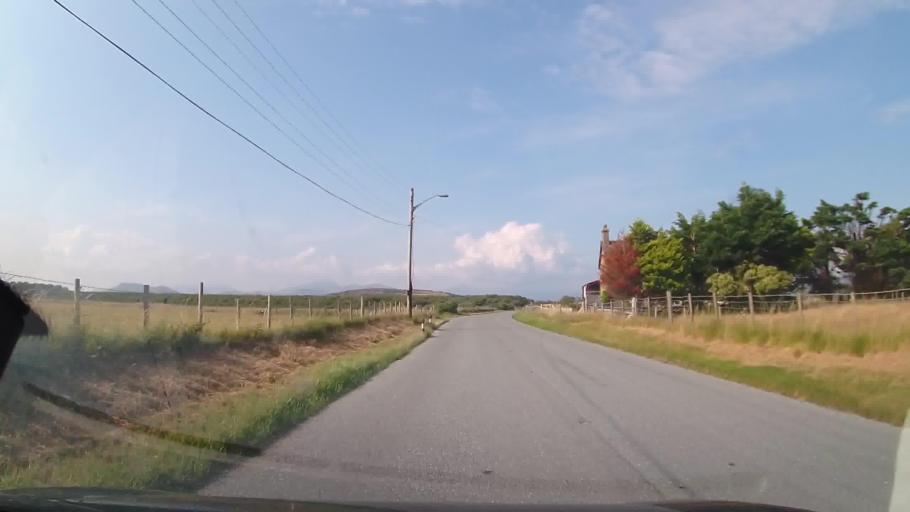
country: GB
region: Wales
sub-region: Gwynedd
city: Llanfair
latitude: 52.8740
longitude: -4.1051
